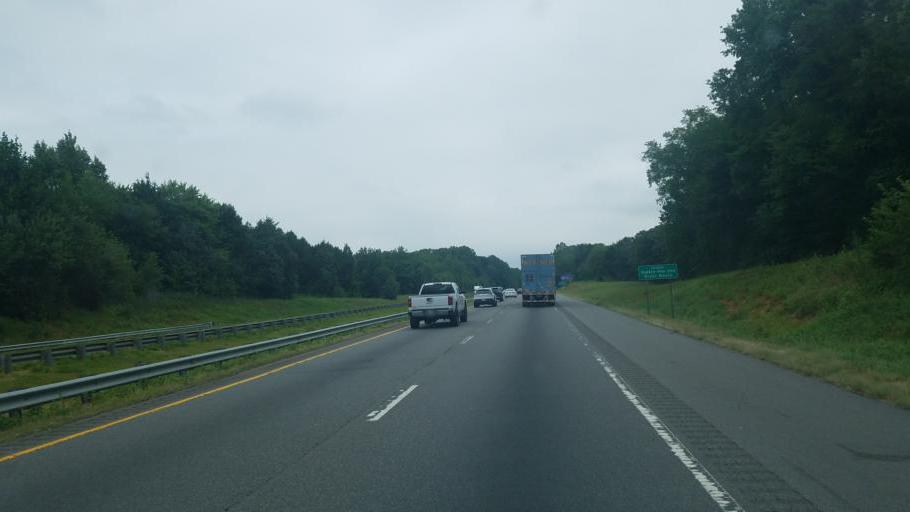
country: US
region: North Carolina
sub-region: Iredell County
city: Troutman
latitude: 35.6617
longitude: -80.8602
